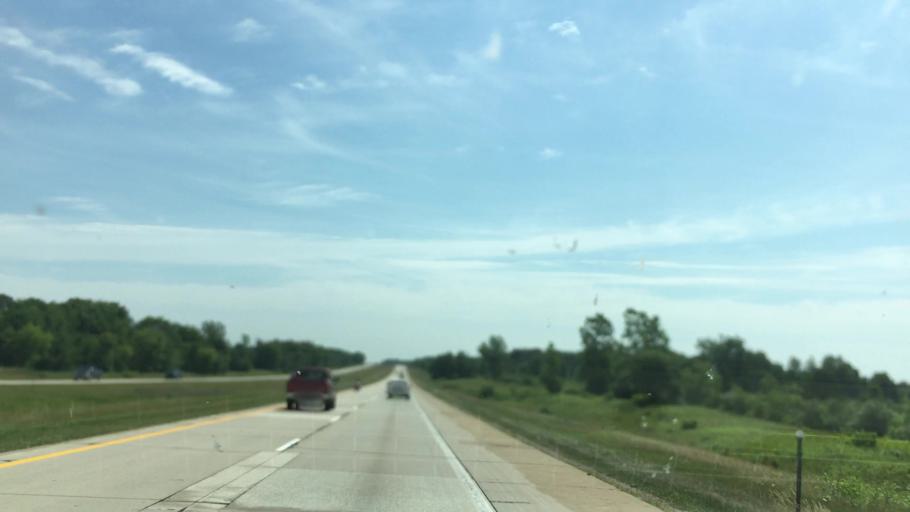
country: US
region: Michigan
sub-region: Lapeer County
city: Imlay City
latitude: 42.9965
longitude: -83.1189
